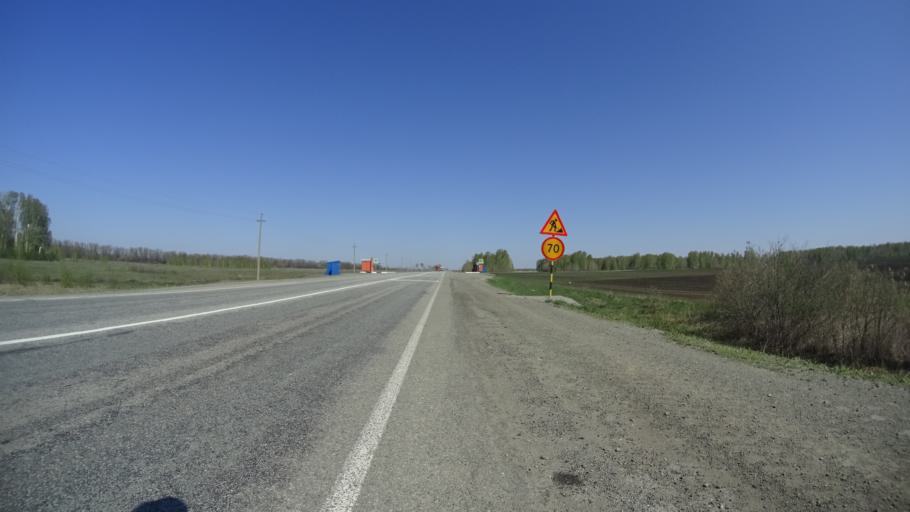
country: RU
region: Chelyabinsk
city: Troitsk
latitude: 54.1872
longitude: 61.4340
